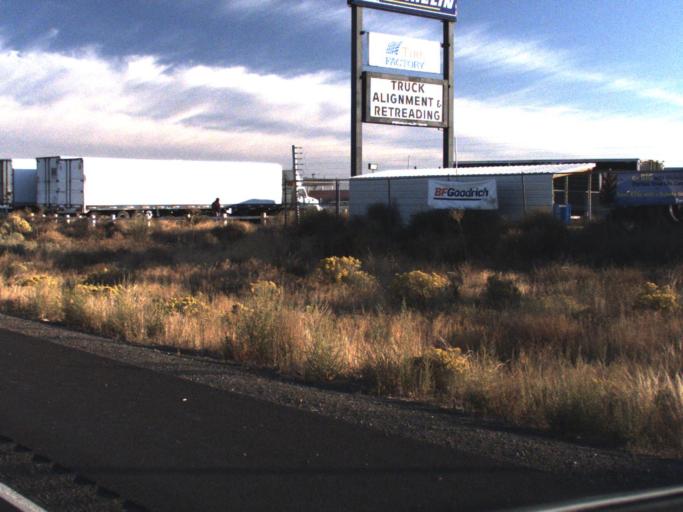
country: US
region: Washington
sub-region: Franklin County
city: Pasco
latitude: 46.2602
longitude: -119.0849
